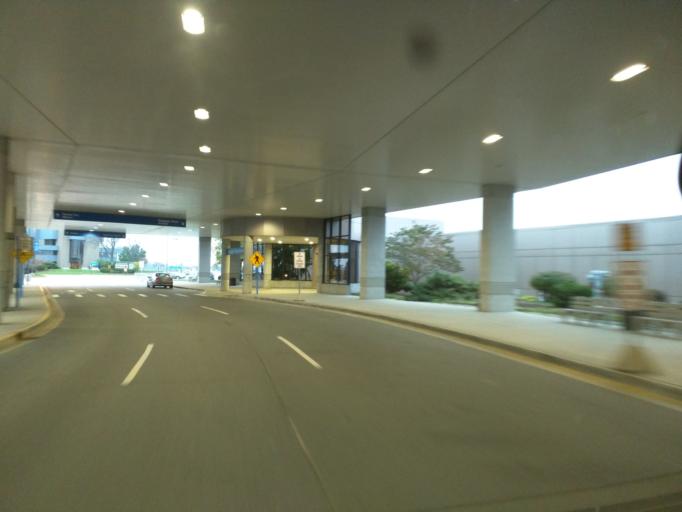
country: US
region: Michigan
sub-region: Ingham County
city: Edgemont Park
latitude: 42.7747
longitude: -84.5895
